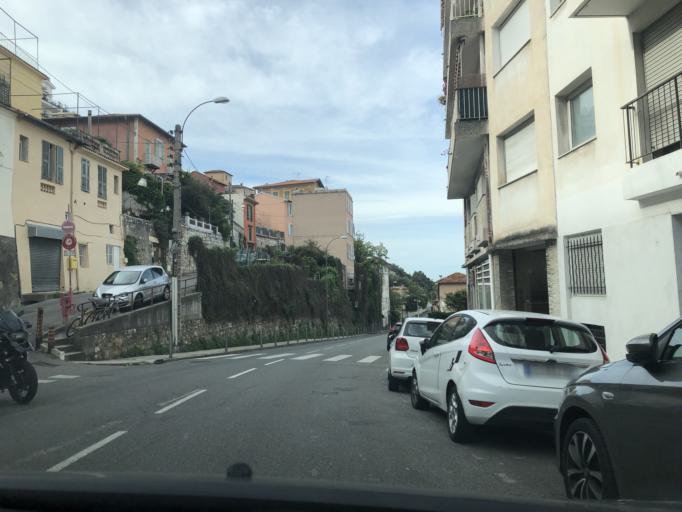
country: FR
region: Provence-Alpes-Cote d'Azur
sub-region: Departement des Alpes-Maritimes
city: Villefranche-sur-Mer
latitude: 43.7123
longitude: 7.2958
